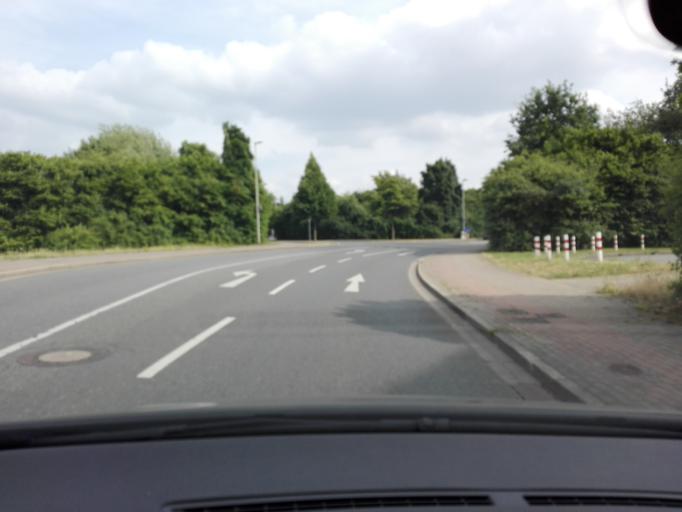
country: DE
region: North Rhine-Westphalia
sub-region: Regierungsbezirk Arnsberg
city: Unna
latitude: 51.5390
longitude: 7.6727
